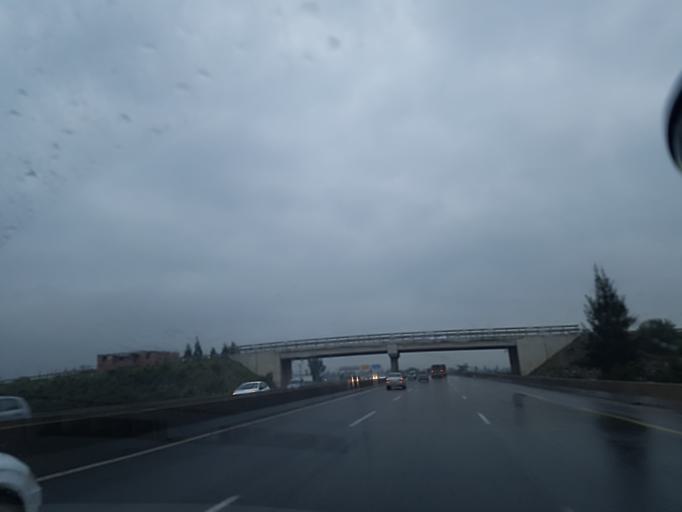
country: DZ
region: Blida
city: Meftah
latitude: 36.6551
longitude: 3.2470
